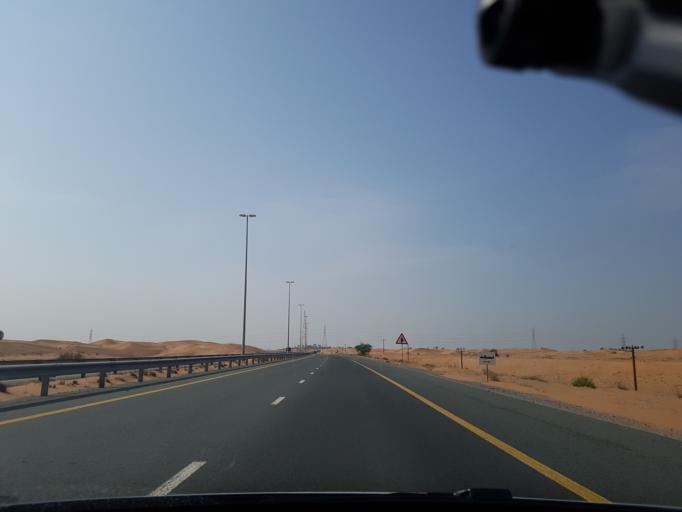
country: AE
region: Umm al Qaywayn
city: Umm al Qaywayn
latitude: 25.5229
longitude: 55.7361
